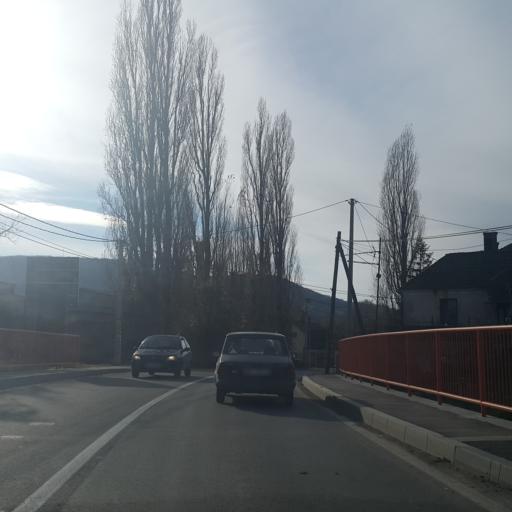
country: RS
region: Central Serbia
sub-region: Sumadijski Okrug
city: Arangelovac
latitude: 44.3353
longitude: 20.4555
